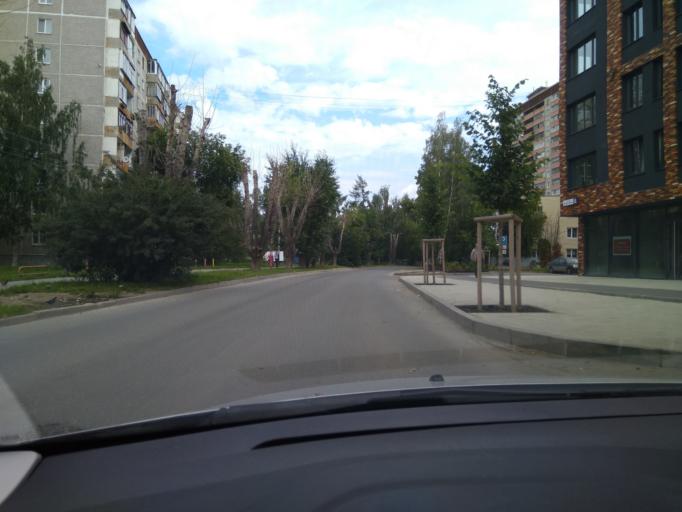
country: RU
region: Sverdlovsk
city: Yekaterinburg
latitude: 56.9091
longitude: 60.6004
